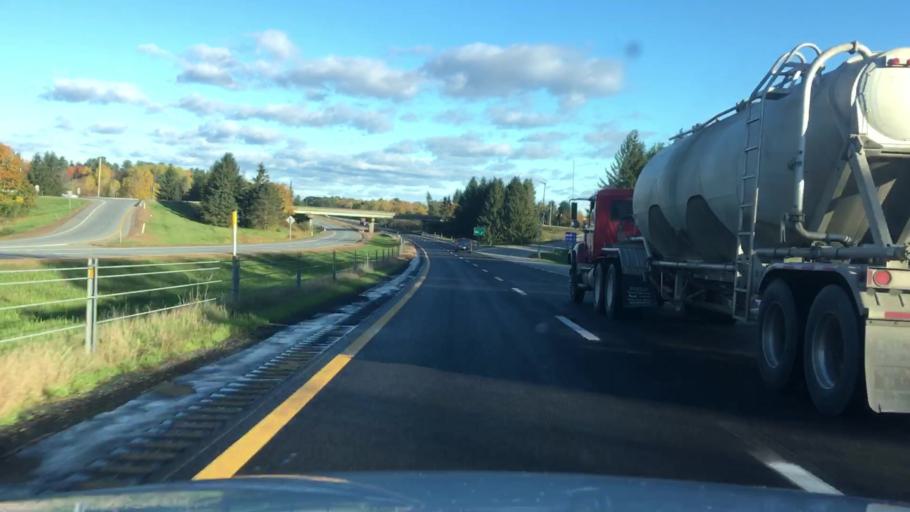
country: US
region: Maine
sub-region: Penobscot County
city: Orono
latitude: 44.9001
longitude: -68.6909
